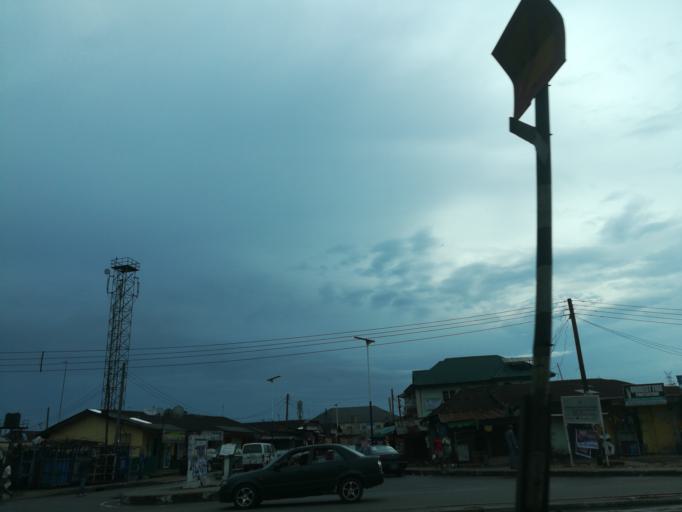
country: NG
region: Rivers
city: Port Harcourt
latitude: 4.7999
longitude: 7.0062
